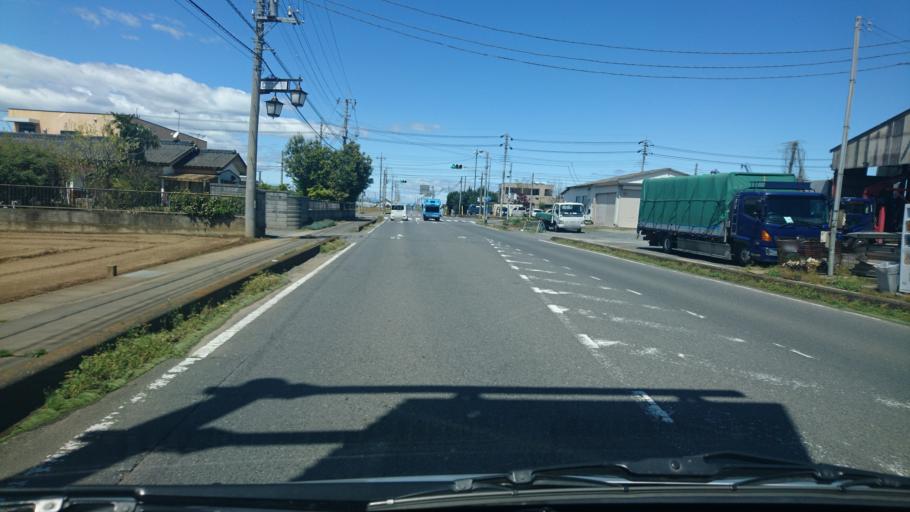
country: JP
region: Ibaraki
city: Shimodate
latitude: 36.2540
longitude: 139.9517
